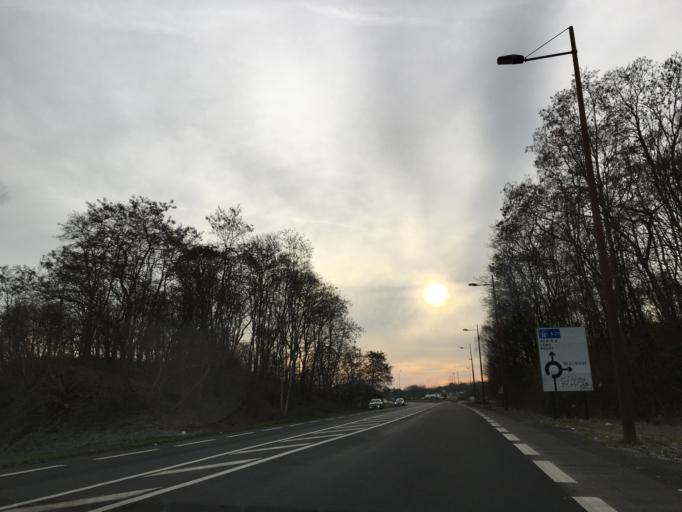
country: FR
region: Nord-Pas-de-Calais
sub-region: Departement du Pas-de-Calais
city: Montigny-en-Gohelle
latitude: 50.4368
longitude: 2.9491
